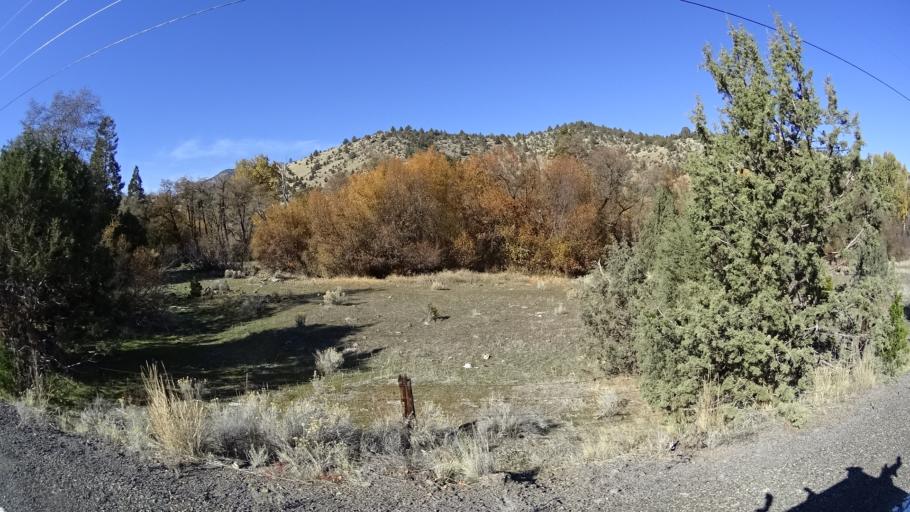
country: US
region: California
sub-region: Siskiyou County
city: Weed
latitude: 41.4759
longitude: -122.5768
